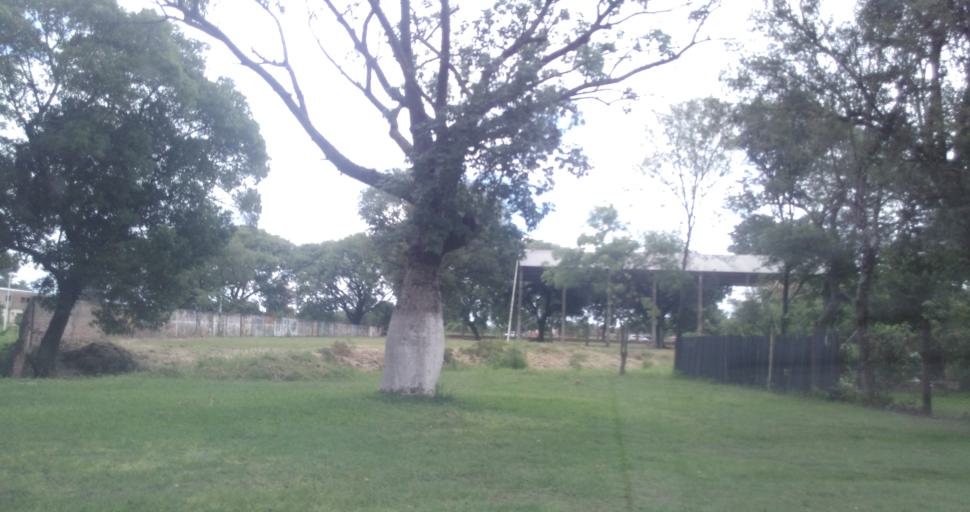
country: AR
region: Chaco
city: Fontana
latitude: -27.4204
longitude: -59.0331
